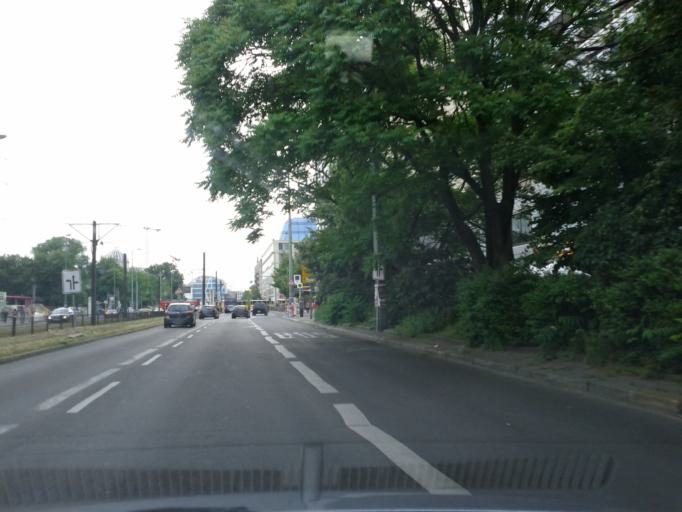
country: DE
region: Berlin
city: Mitte
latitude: 52.5213
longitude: 13.4068
